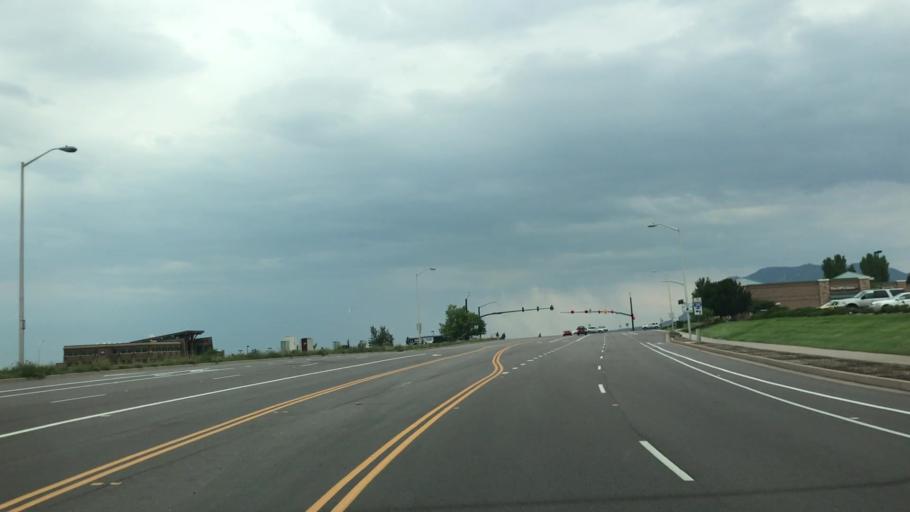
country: US
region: Colorado
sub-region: El Paso County
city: Colorado Springs
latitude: 38.8781
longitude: -104.8471
